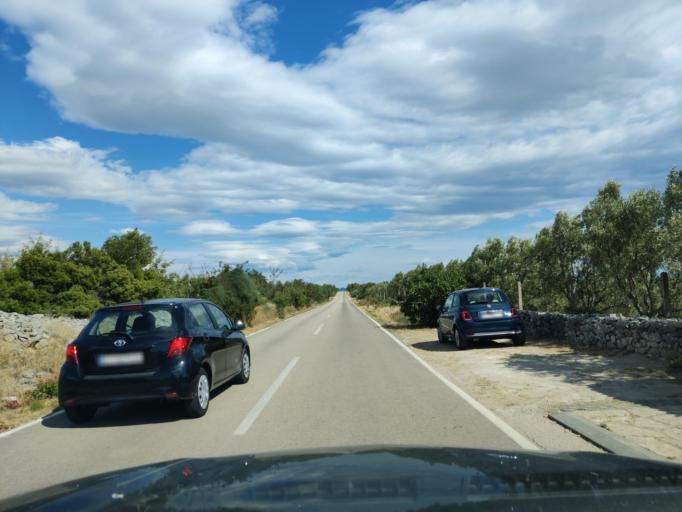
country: HR
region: Sibensko-Kniniska
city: Zaton
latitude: 43.7548
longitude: 15.8321
